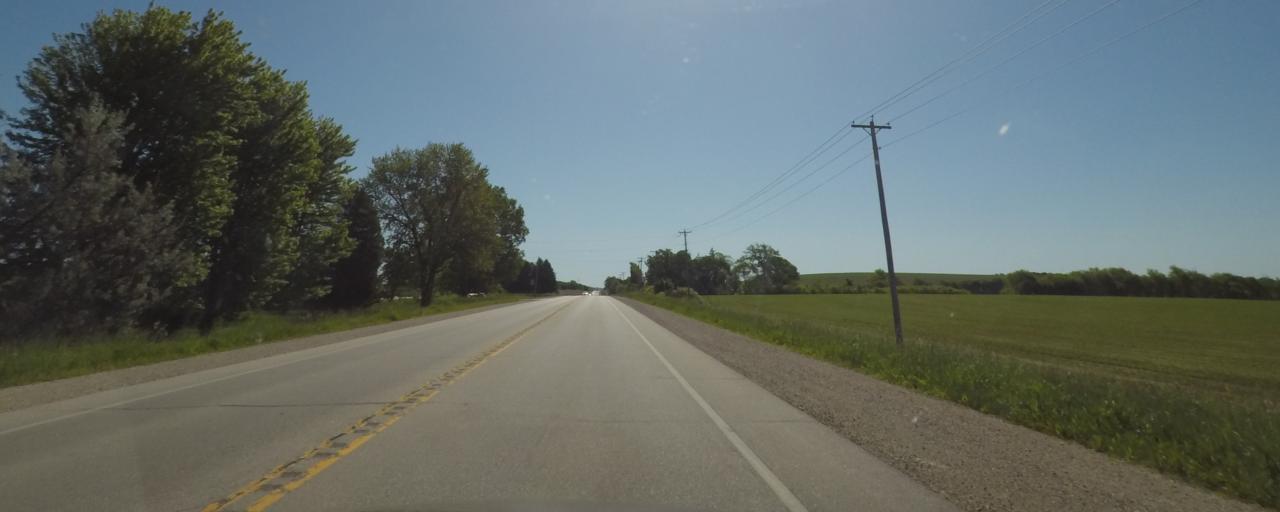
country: US
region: Wisconsin
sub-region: Fond du Lac County
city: Saint Peter
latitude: 43.7836
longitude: -88.3593
